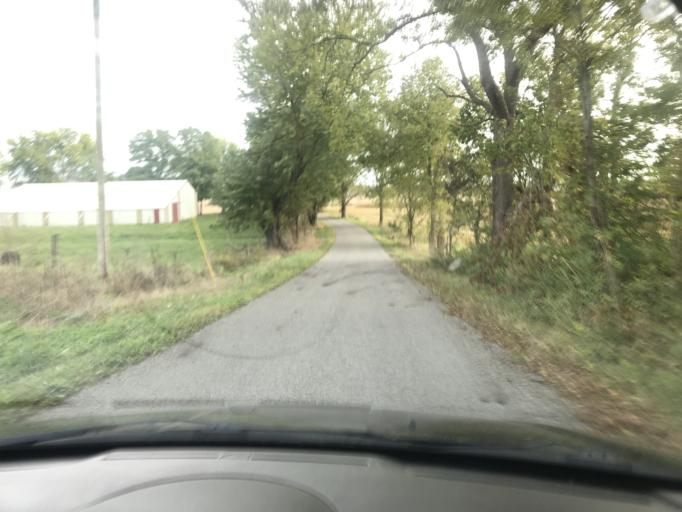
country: US
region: Ohio
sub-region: Logan County
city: West Liberty
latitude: 40.2410
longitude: -83.6876
